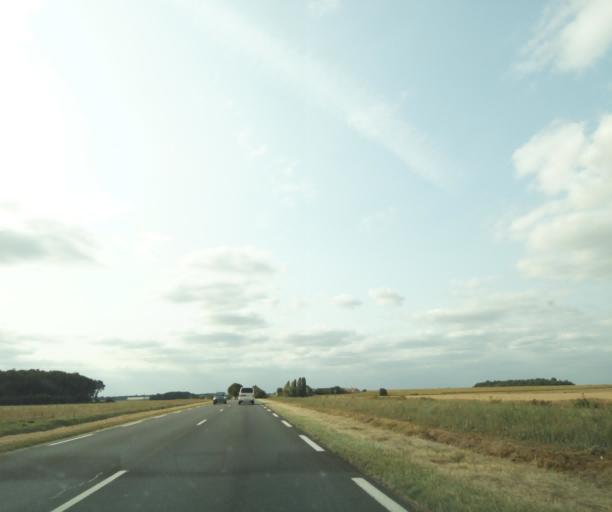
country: FR
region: Centre
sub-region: Departement d'Indre-et-Loire
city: Truyes
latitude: 47.2418
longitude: 0.8615
